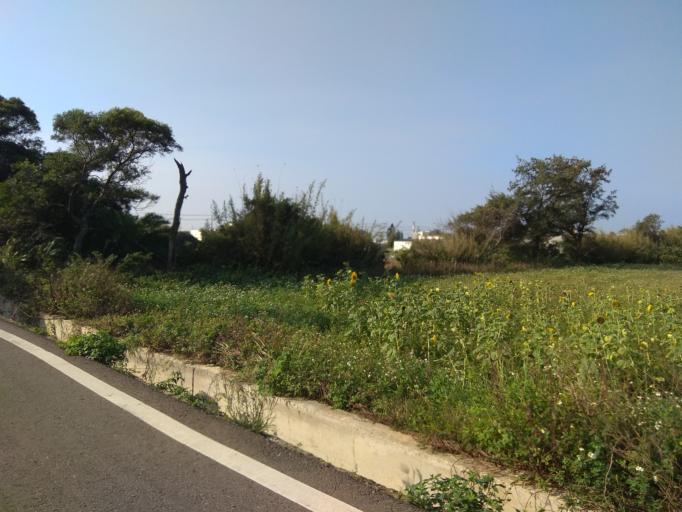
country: TW
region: Taiwan
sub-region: Hsinchu
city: Zhubei
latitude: 24.9894
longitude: 121.0366
